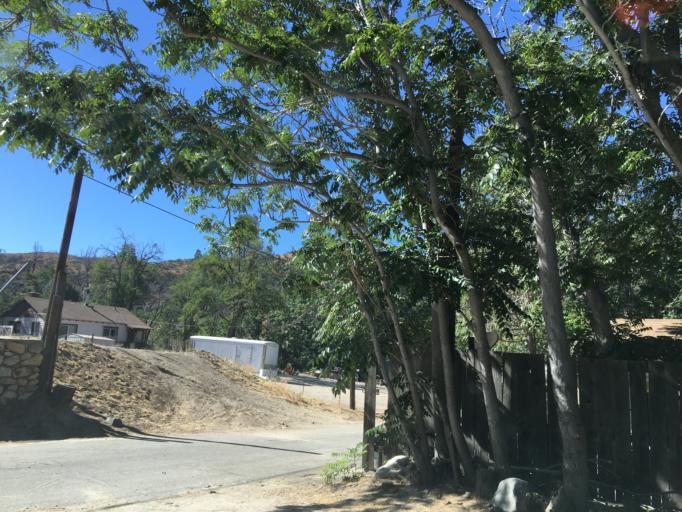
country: US
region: California
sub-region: Los Angeles County
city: Green Valley
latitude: 34.6749
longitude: -118.4405
